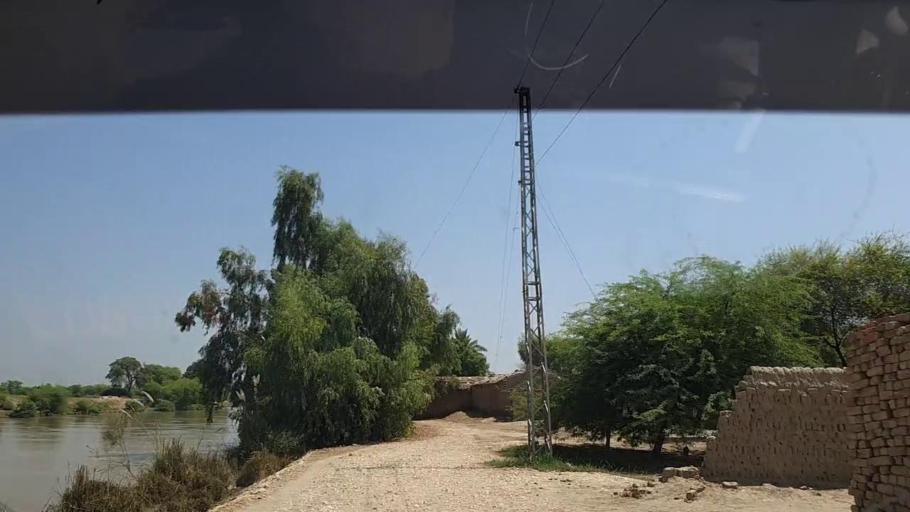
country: PK
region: Sindh
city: Ghauspur
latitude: 28.1650
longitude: 69.1304
